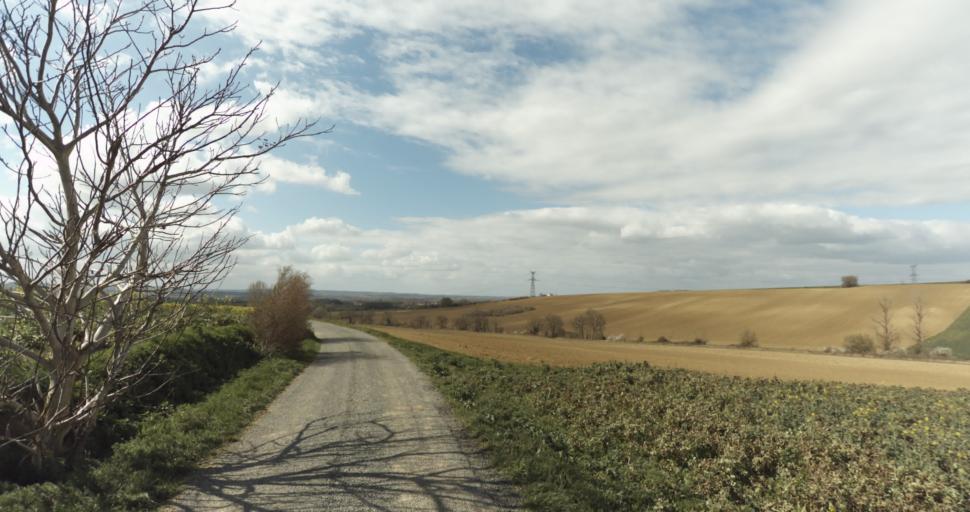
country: FR
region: Midi-Pyrenees
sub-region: Departement de la Haute-Garonne
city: Auterive
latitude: 43.3855
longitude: 1.4791
